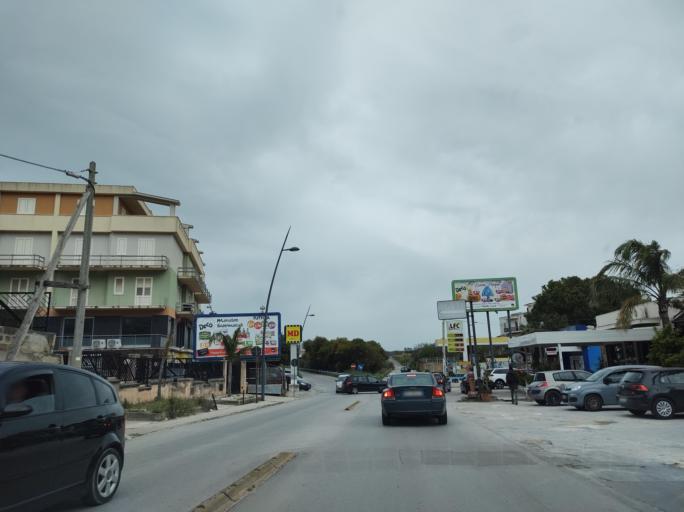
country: IT
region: Sicily
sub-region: Trapani
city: Castellammare del Golfo
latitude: 38.0160
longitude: 12.8912
